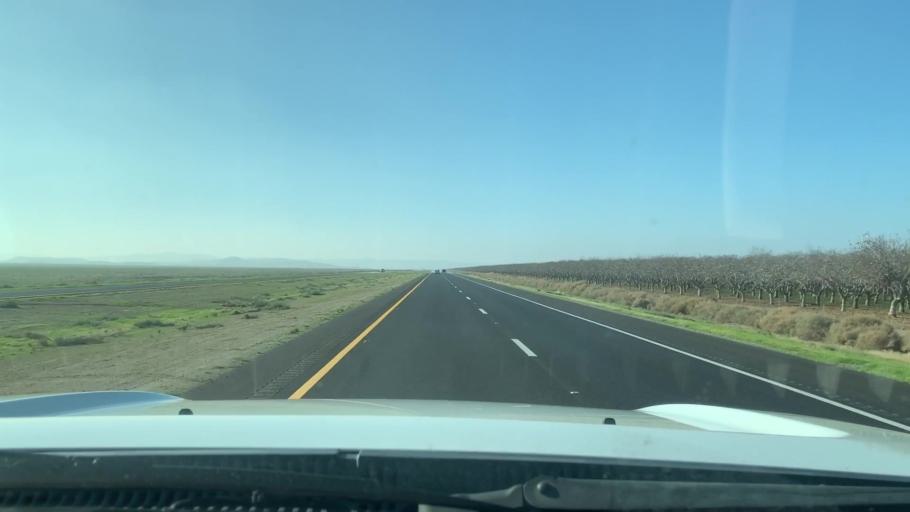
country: US
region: California
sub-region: Kern County
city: Lost Hills
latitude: 35.6148
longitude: -119.9077
